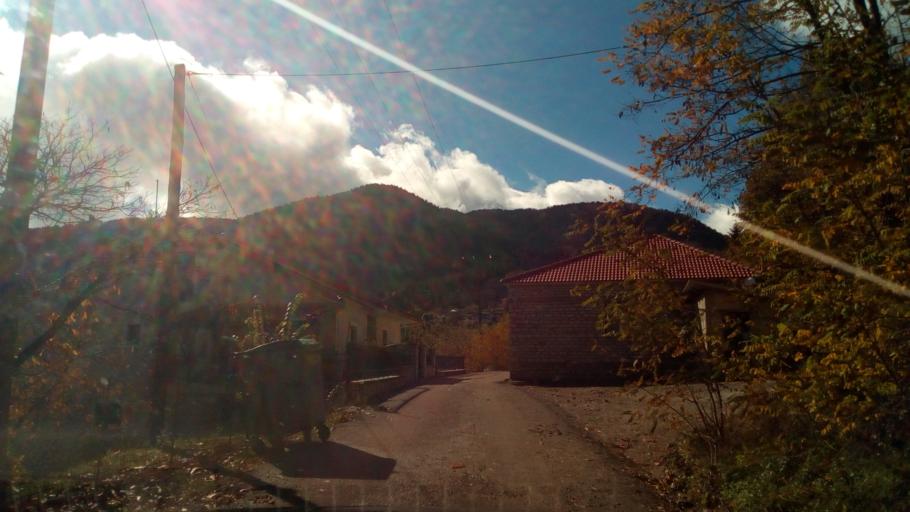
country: GR
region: West Greece
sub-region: Nomos Aitolias kai Akarnanias
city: Nafpaktos
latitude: 38.5947
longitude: 21.9254
